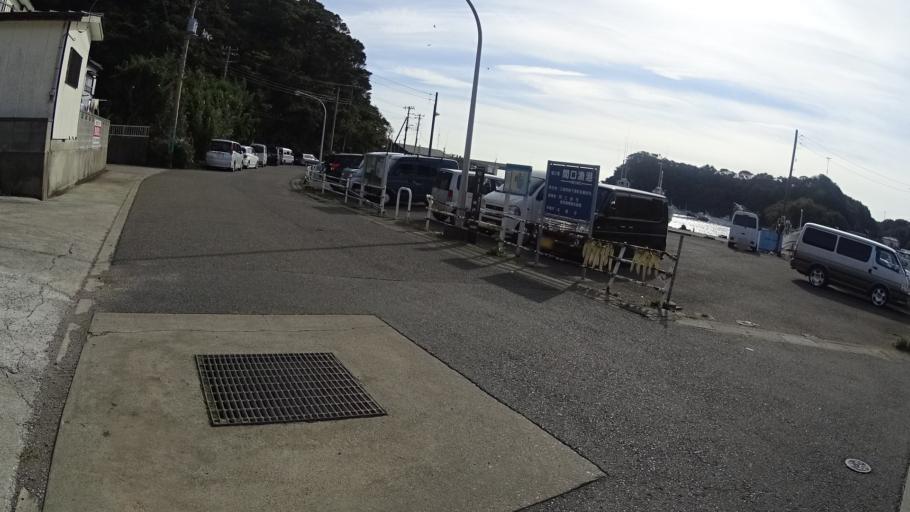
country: JP
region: Kanagawa
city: Miura
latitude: 35.1462
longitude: 139.6774
